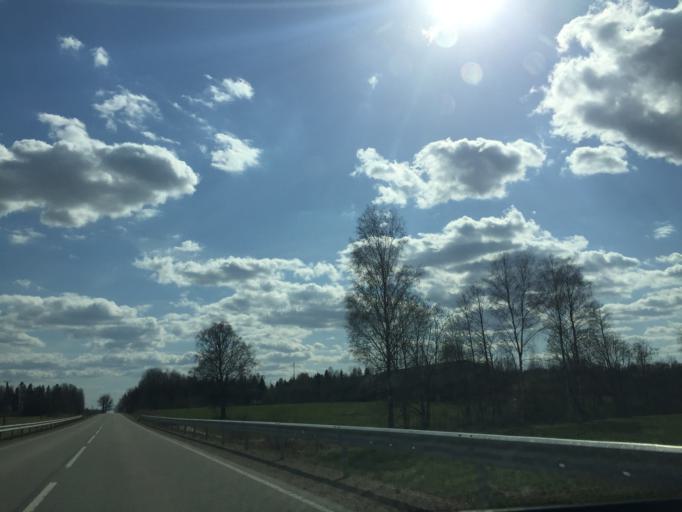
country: LV
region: Skriveri
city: Skriveri
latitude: 56.7472
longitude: 25.1671
